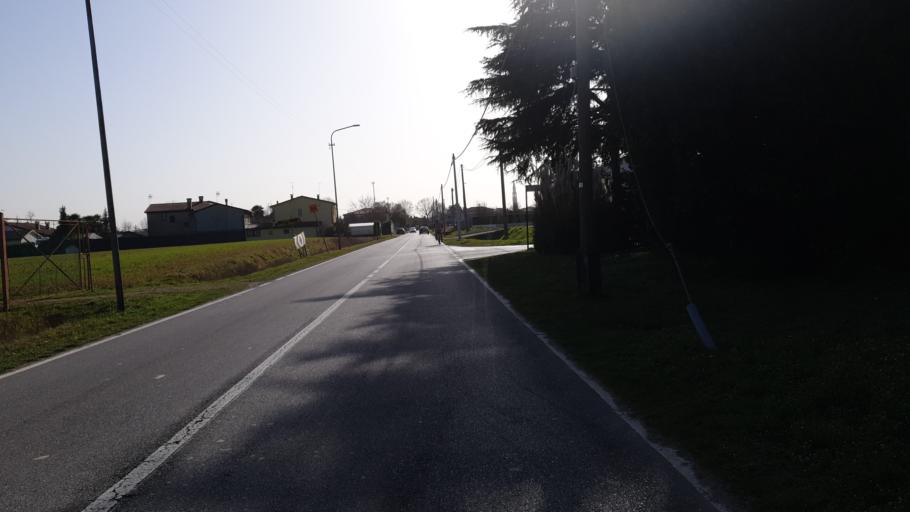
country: IT
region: Veneto
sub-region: Provincia di Padova
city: Vigodarzere
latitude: 45.4655
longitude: 11.8900
